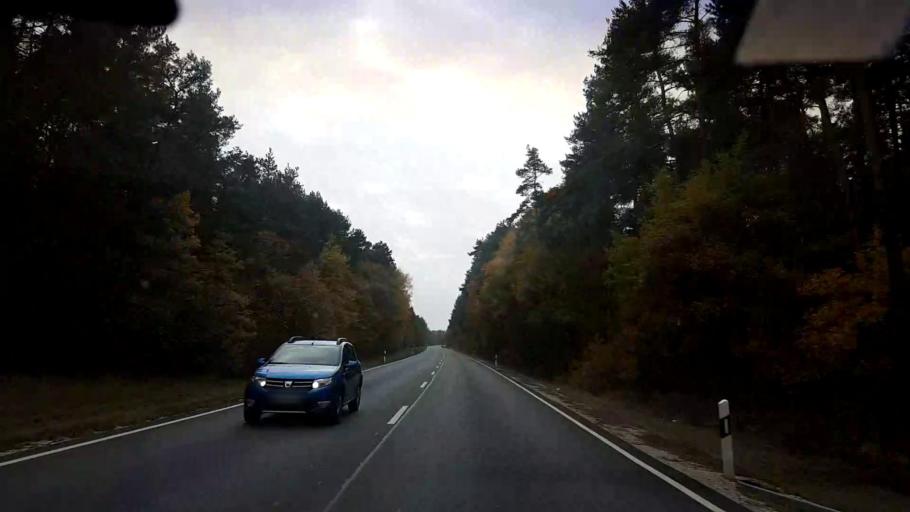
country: DE
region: Bavaria
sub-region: Upper Franconia
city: Pettstadt
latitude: 49.7906
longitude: 10.9290
